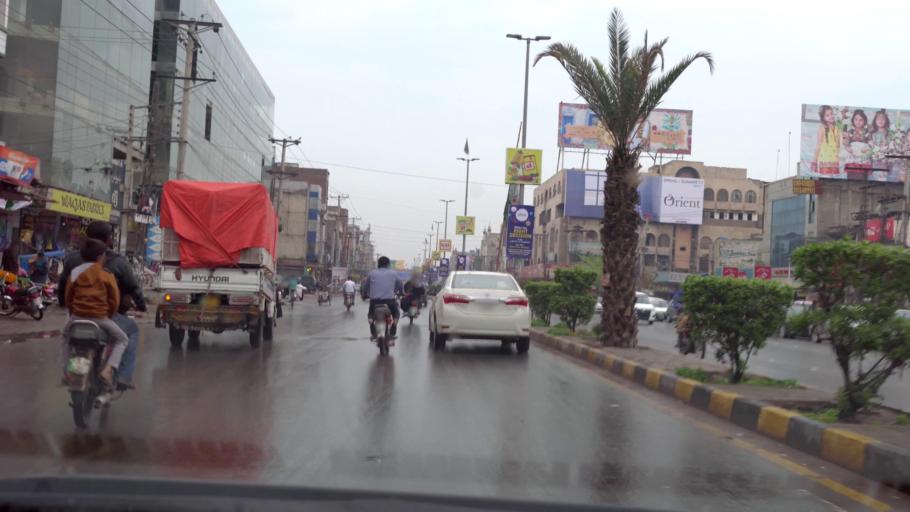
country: PK
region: Punjab
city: Faisalabad
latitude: 31.4058
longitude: 73.1011
